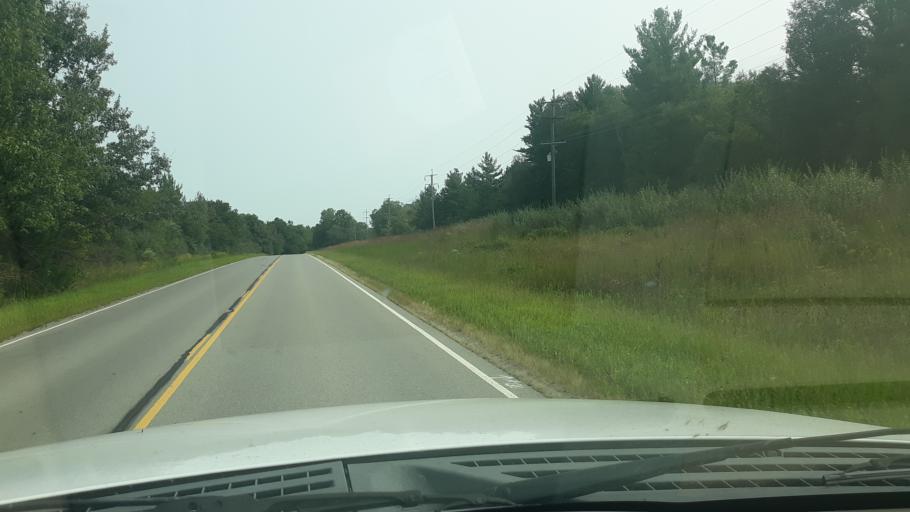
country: US
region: Illinois
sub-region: White County
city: Norris City
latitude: 37.9172
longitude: -88.3534
